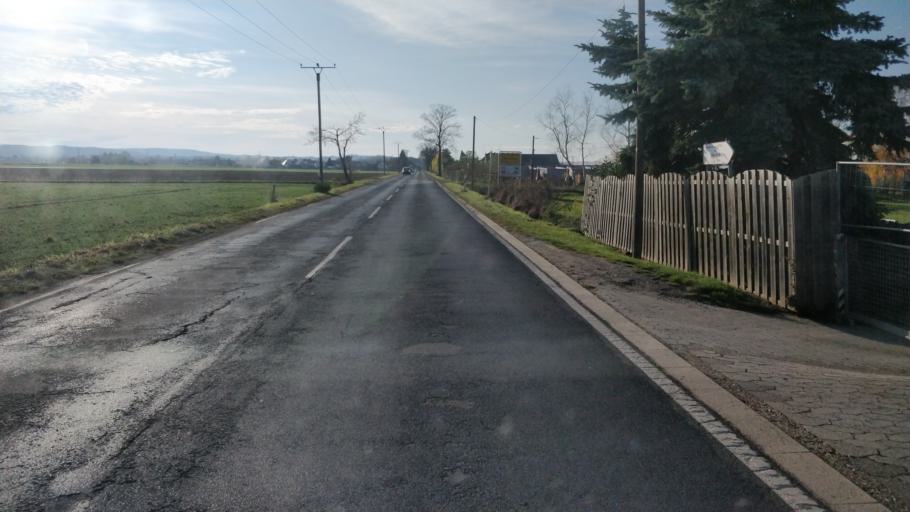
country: DE
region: North Rhine-Westphalia
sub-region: Regierungsbezirk Koln
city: Rheinbach
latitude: 50.6418
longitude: 6.8707
